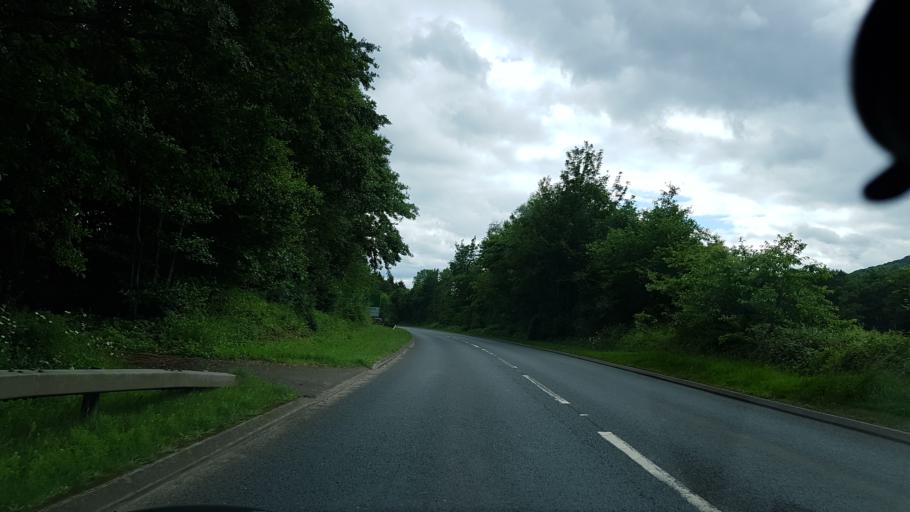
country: GB
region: Wales
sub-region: Monmouthshire
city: Abergavenny
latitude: 51.8538
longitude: -3.0019
